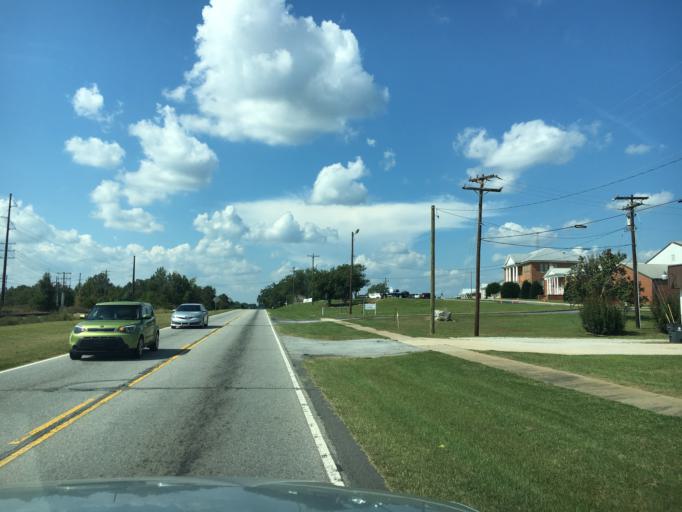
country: US
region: South Carolina
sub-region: Greenville County
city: Fountain Inn
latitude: 34.6180
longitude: -82.1224
